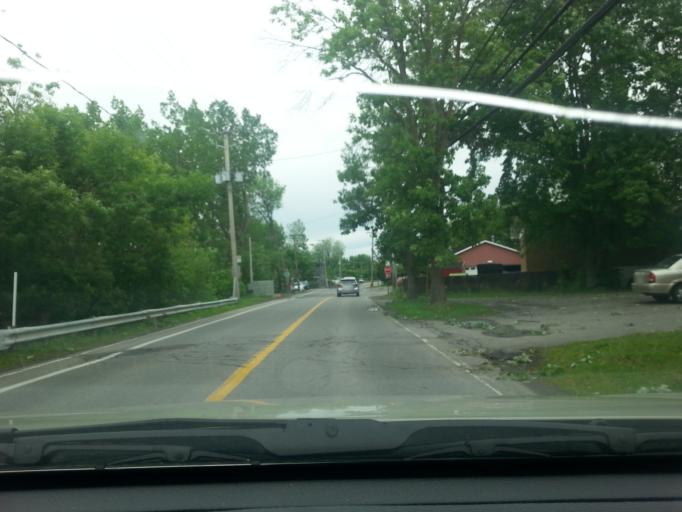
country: CA
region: Quebec
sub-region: Lanaudiere
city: Terrebonne
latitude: 45.6915
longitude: -73.5970
